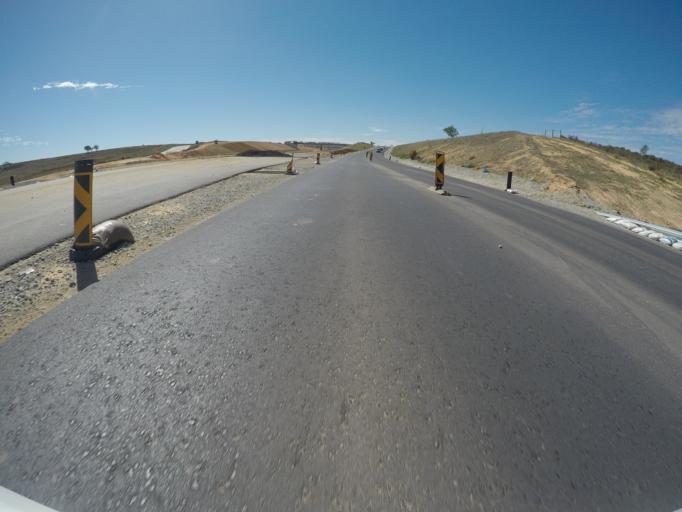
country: ZA
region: Western Cape
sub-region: West Coast District Municipality
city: Malmesbury
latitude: -33.4828
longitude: 18.6769
